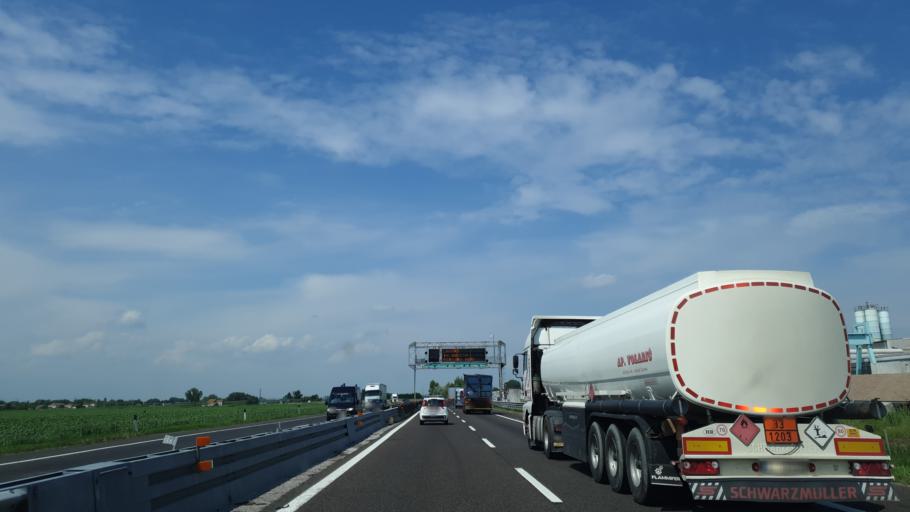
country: IT
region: Emilia-Romagna
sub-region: Provincia di Ferrara
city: San Martino
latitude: 44.7813
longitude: 11.5496
